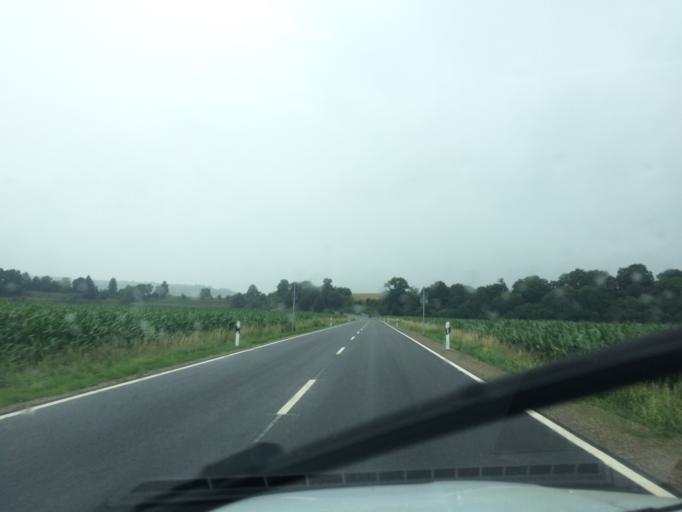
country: DE
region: Hesse
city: Trendelburg
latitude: 51.5812
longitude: 9.4157
